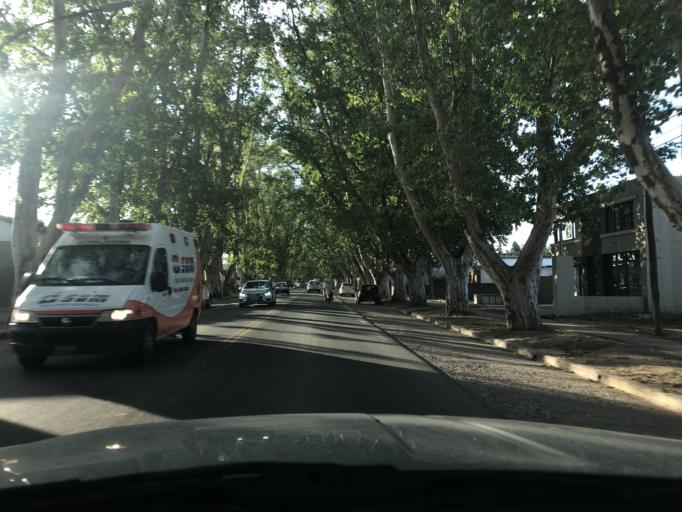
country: AR
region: Cordoba
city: Jesus Maria
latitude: -31.0074
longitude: -64.0780
